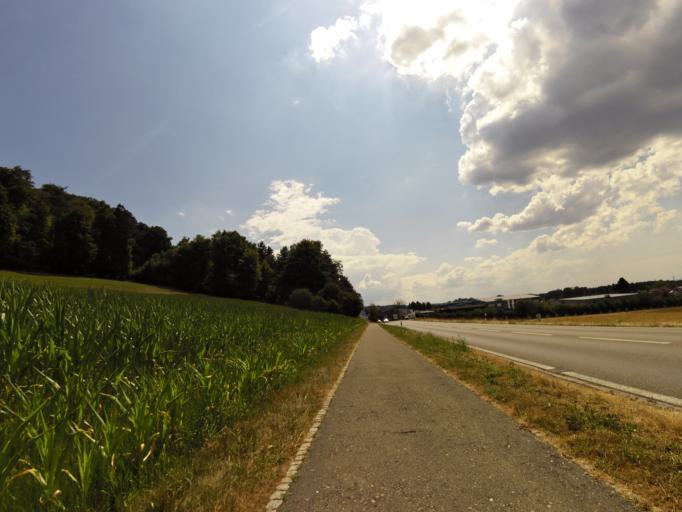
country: CH
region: Aargau
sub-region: Bezirk Lenzburg
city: Othmarsingen
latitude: 47.4084
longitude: 8.2220
